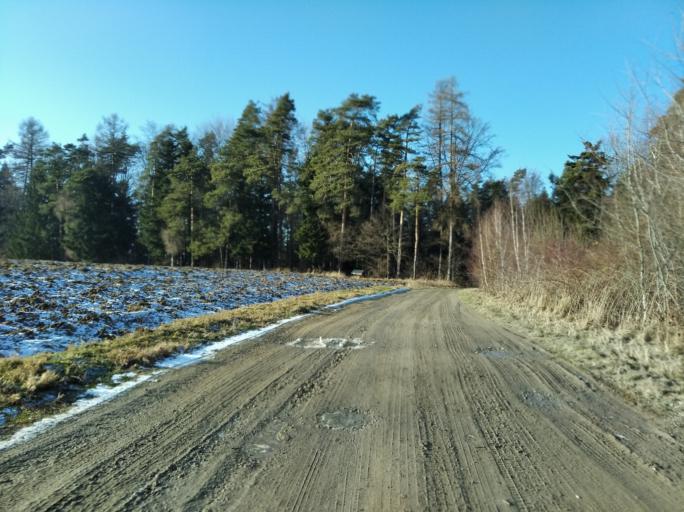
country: PL
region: Subcarpathian Voivodeship
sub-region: Powiat strzyzowski
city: Jawornik
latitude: 49.8311
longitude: 21.8594
